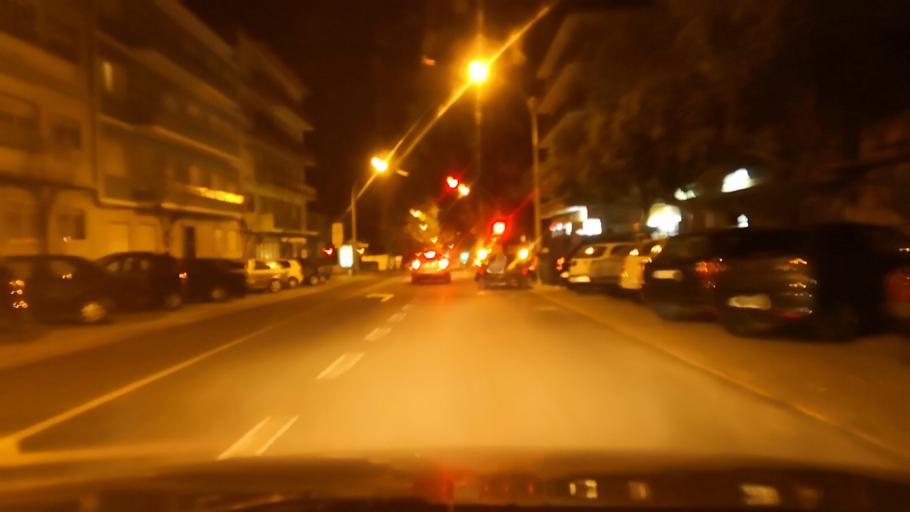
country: PT
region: Setubal
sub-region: Setubal
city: Setubal
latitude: 38.5353
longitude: -8.8936
